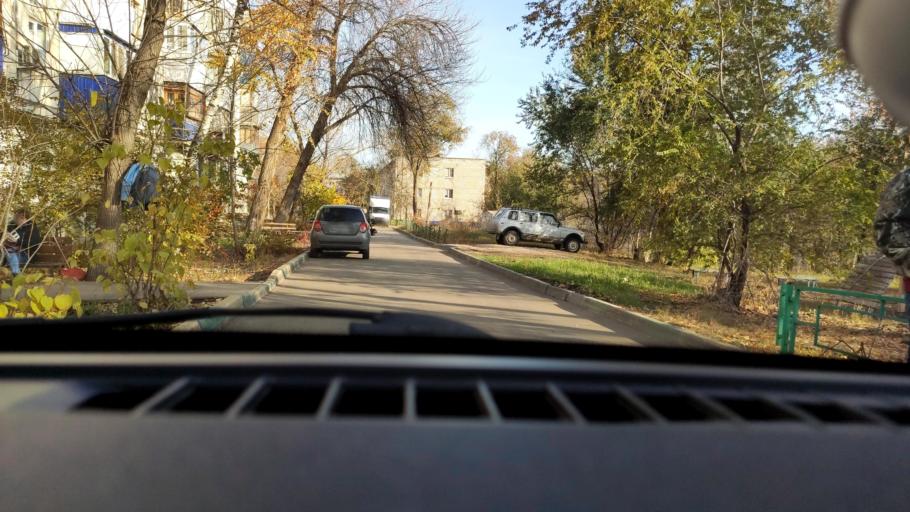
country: RU
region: Samara
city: Samara
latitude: 53.2006
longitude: 50.2105
